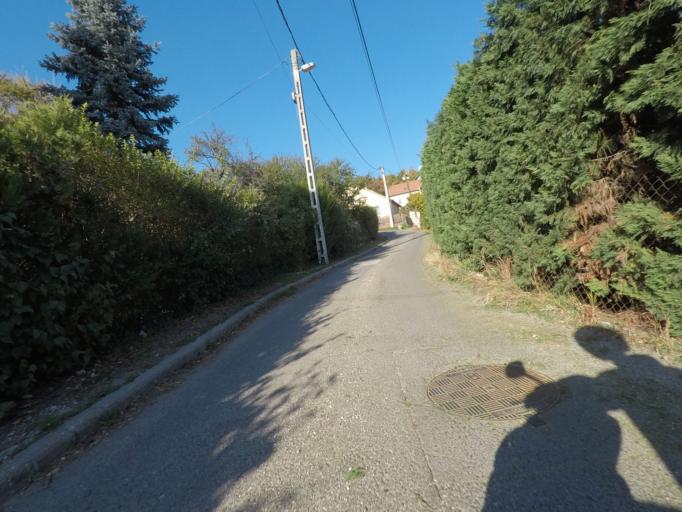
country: HU
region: Pest
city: Nagykovacsi
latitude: 47.6532
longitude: 19.0041
